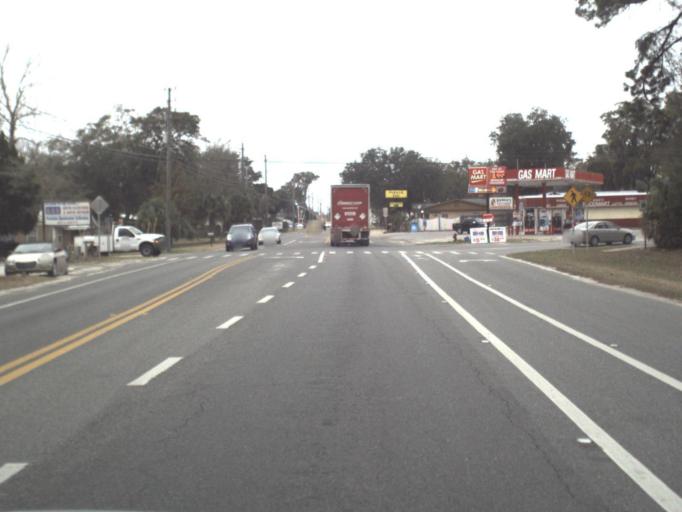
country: US
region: Florida
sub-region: Bay County
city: Parker
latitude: 30.1311
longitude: -85.5989
